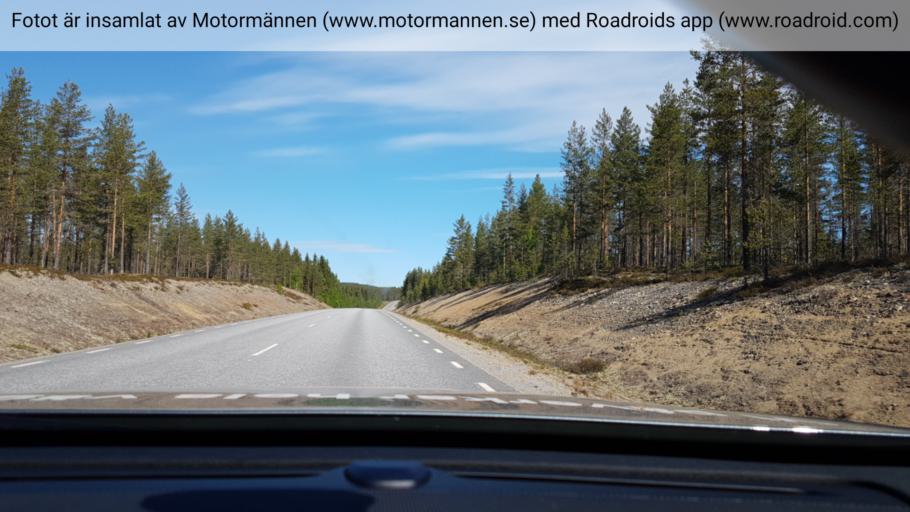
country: SE
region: Vaesterbotten
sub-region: Bjurholms Kommun
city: Bjurholm
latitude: 63.9862
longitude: 18.8038
